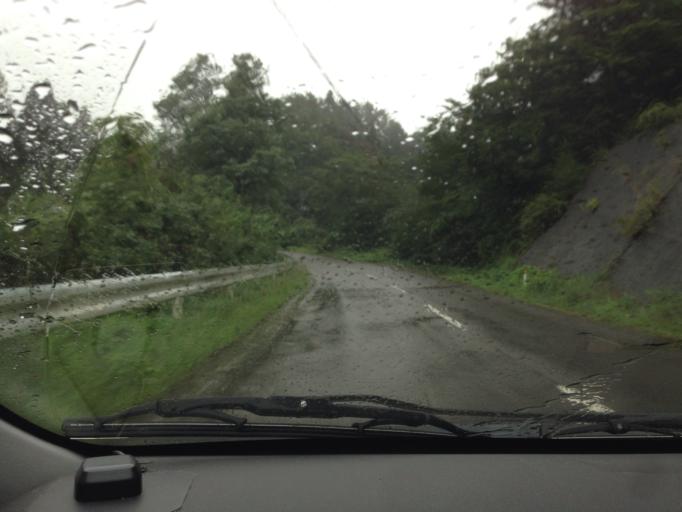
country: JP
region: Fukushima
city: Koriyama
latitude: 37.4332
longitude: 140.2655
